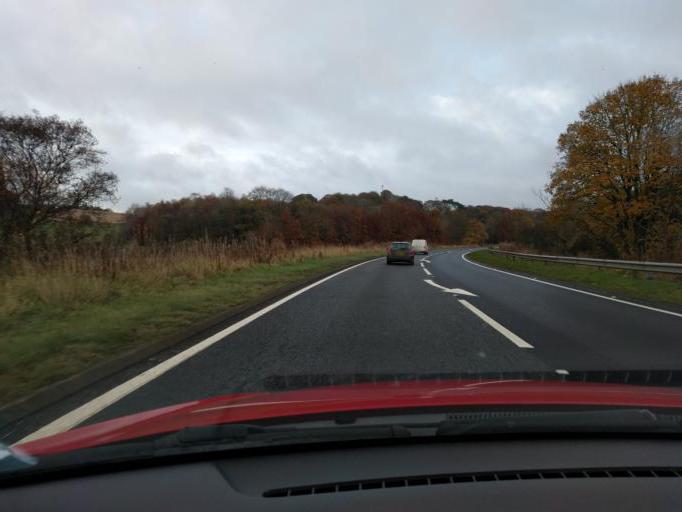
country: GB
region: Scotland
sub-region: The Scottish Borders
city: Chirnside
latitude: 55.8830
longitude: -2.2938
